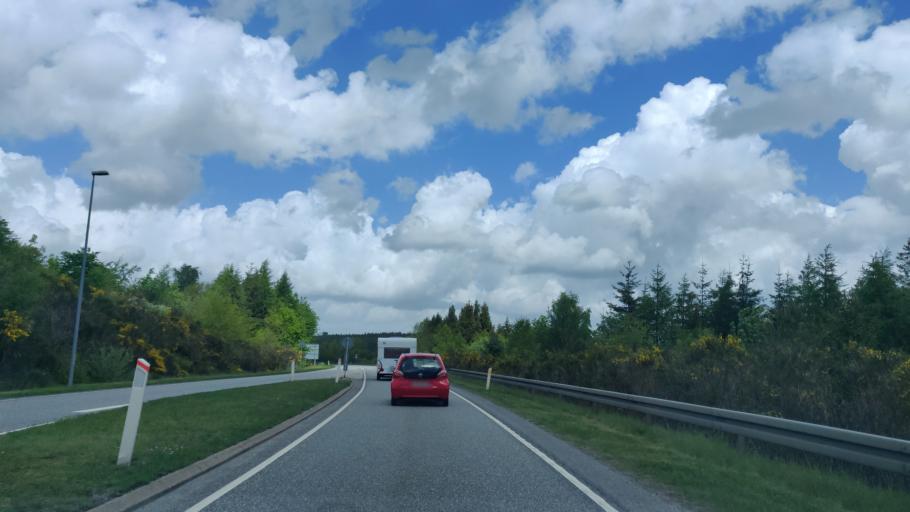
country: DK
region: Central Jutland
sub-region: Hedensted Kommune
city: Torring
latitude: 55.9630
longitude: 9.4056
